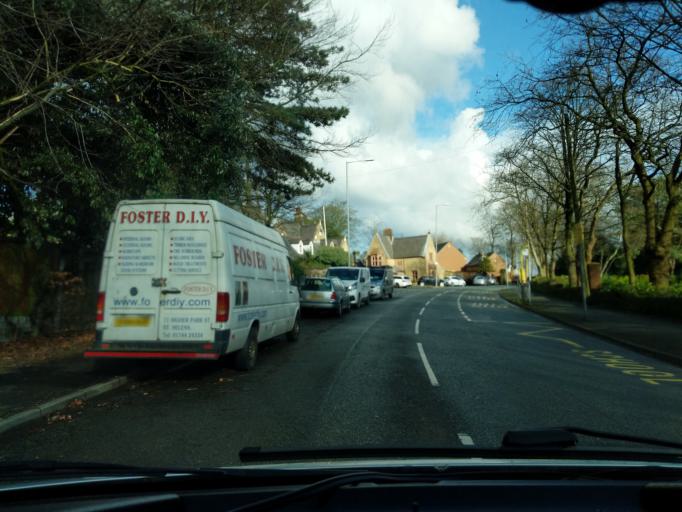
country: GB
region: England
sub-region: St. Helens
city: St Helens
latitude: 53.4649
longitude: -2.7560
